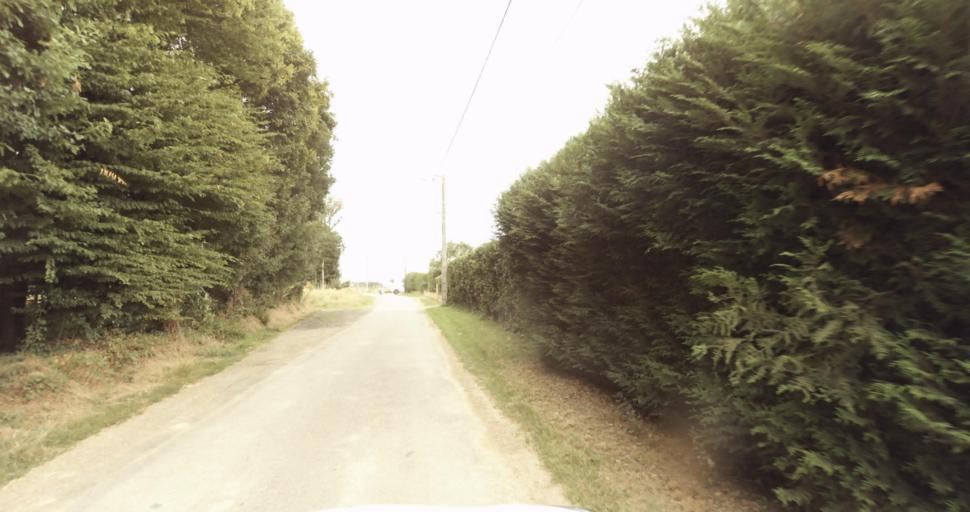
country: FR
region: Haute-Normandie
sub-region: Departement de l'Eure
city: Nonancourt
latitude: 48.7891
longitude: 1.1452
